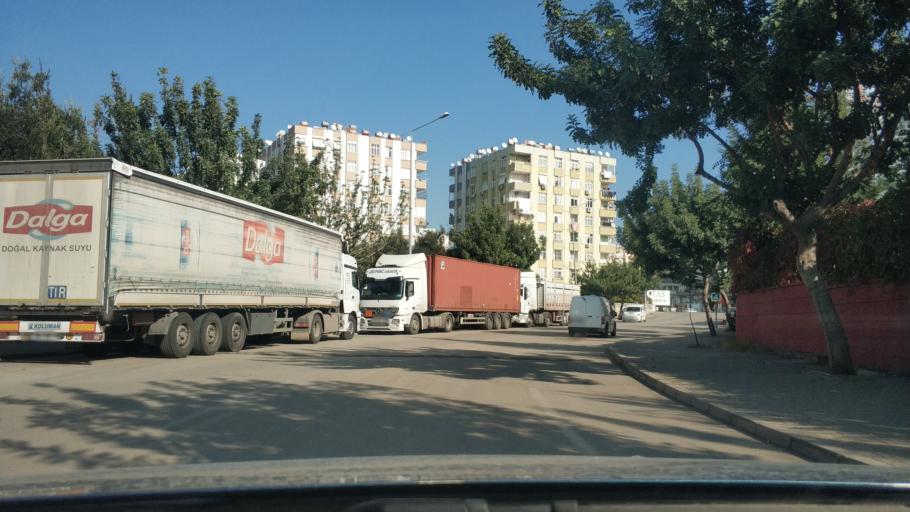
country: TR
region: Adana
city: Seyhan
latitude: 37.0220
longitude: 35.2912
